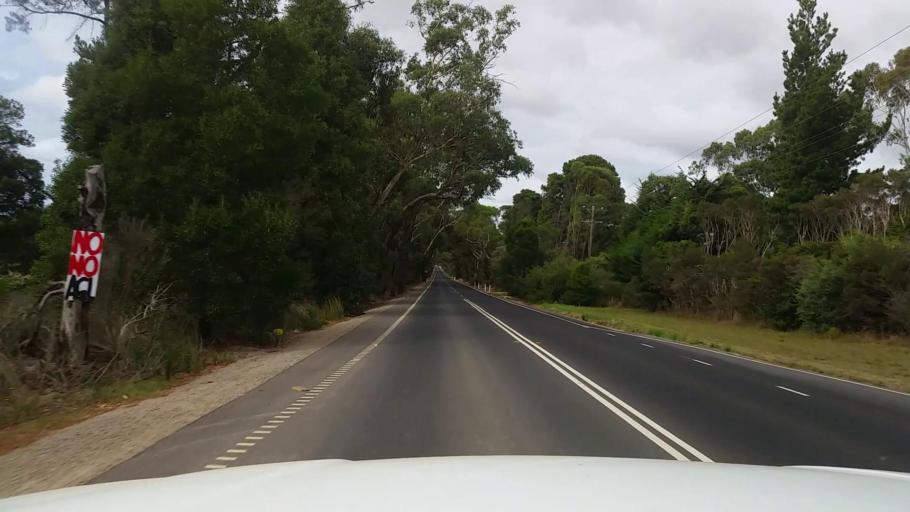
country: AU
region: Victoria
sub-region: Mornington Peninsula
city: Balnarring
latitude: -38.3454
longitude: 145.1017
